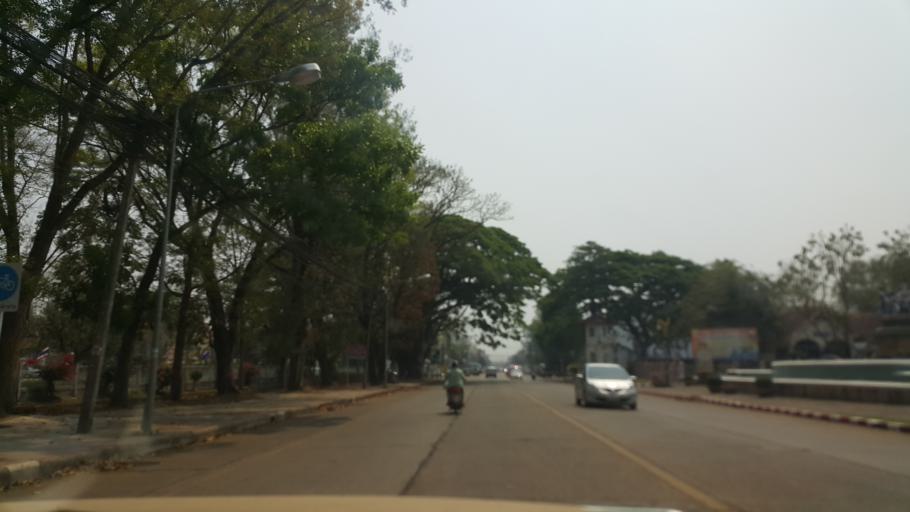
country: TH
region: Nakhon Phanom
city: Nakhon Phanom
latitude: 17.4073
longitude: 104.7813
